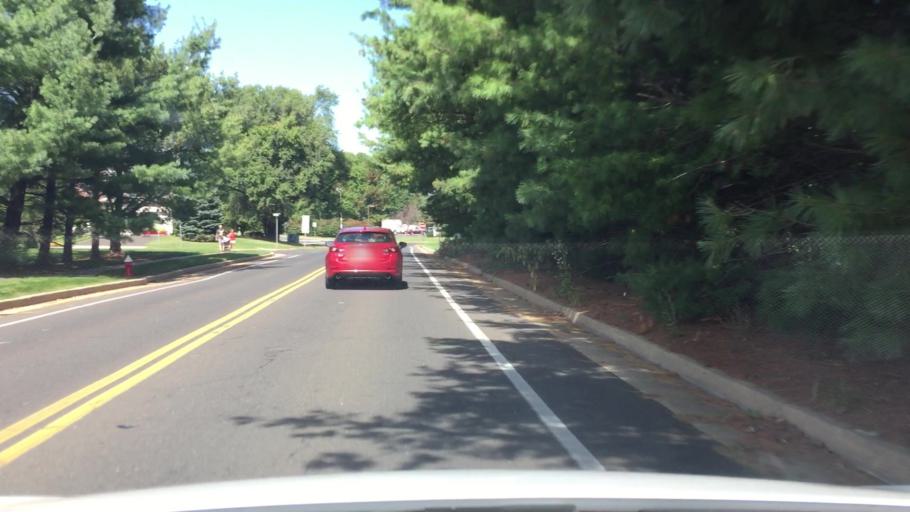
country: US
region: Pennsylvania
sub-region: Bucks County
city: Newtown
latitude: 40.2235
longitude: -74.9196
